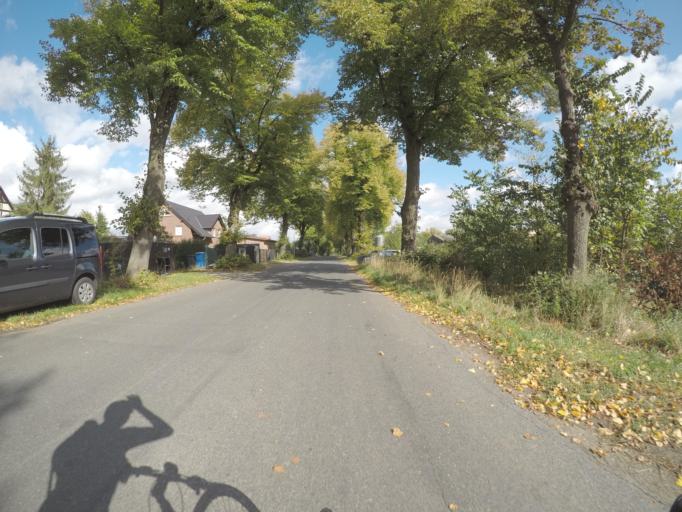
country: DE
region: Brandenburg
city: Ahrensfelde
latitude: 52.5723
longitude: 13.6189
